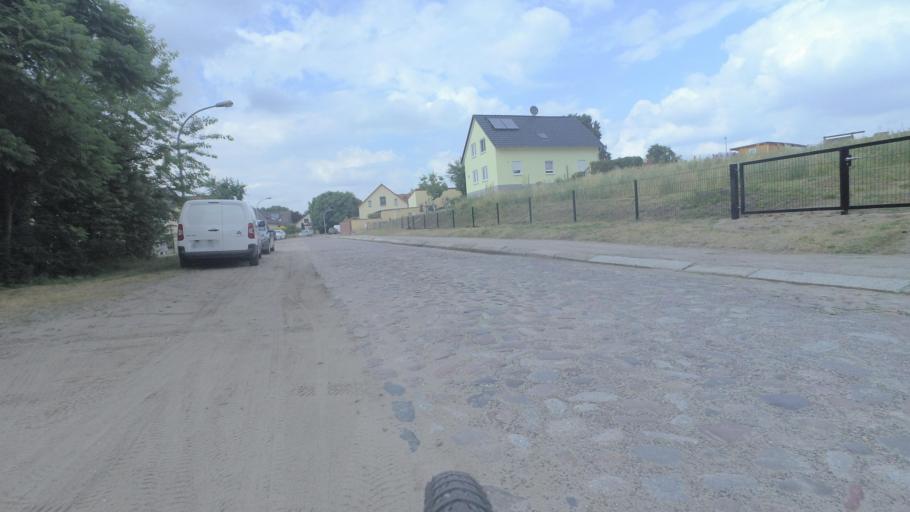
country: DE
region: Brandenburg
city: Zossen
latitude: 52.2066
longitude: 13.4665
